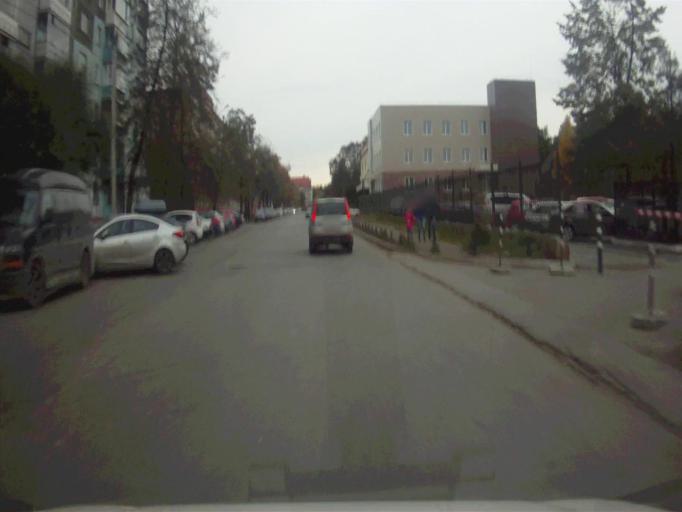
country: RU
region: Chelyabinsk
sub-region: Gorod Chelyabinsk
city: Chelyabinsk
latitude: 55.1621
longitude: 61.3734
